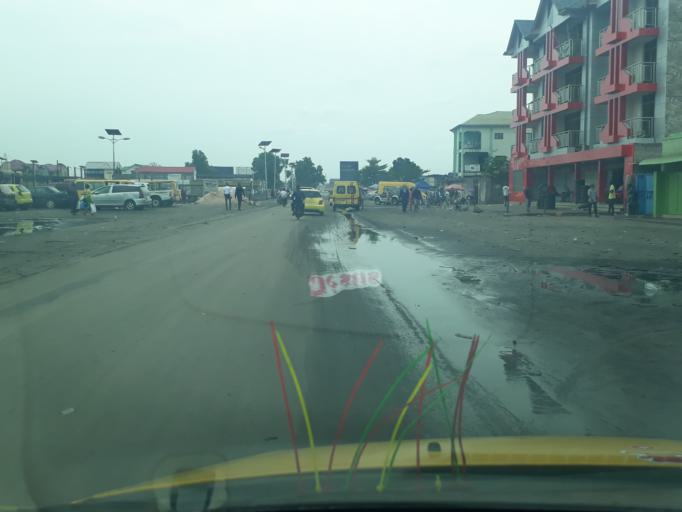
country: CD
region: Kinshasa
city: Kinshasa
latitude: -4.3477
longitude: 15.3019
